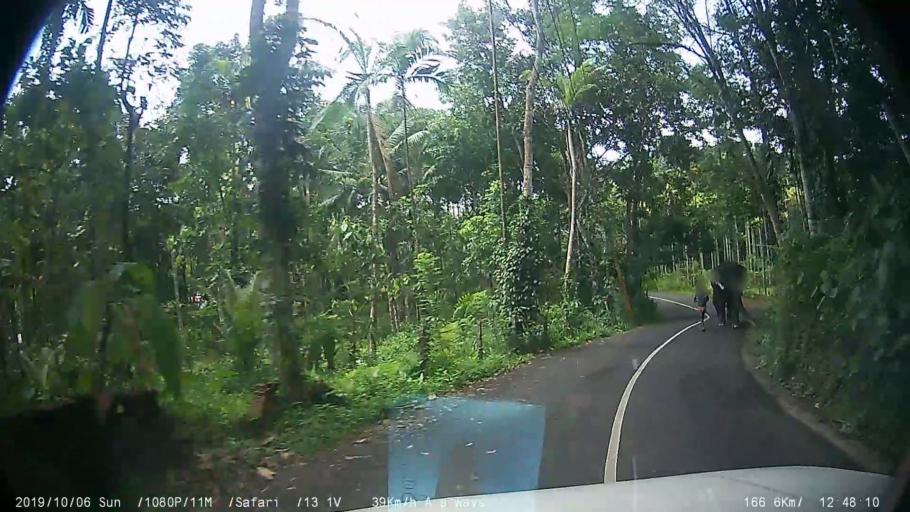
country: IN
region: Kerala
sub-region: Kottayam
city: Palackattumala
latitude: 9.7777
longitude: 76.5981
